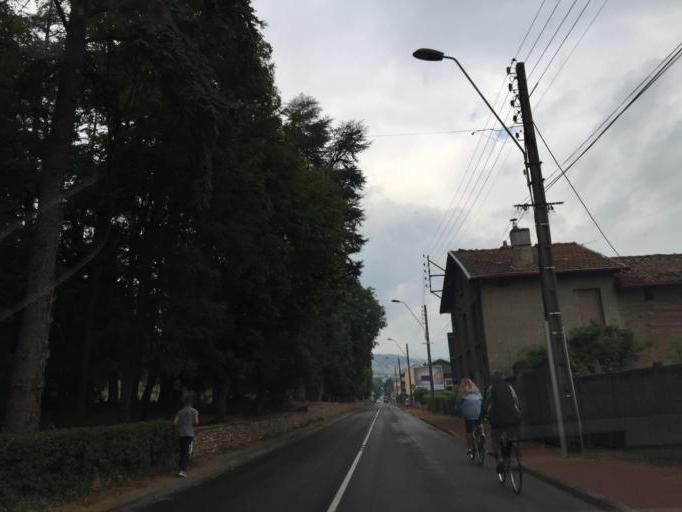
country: FR
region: Rhone-Alpes
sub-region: Departement de la Loire
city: La Talaudiere
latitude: 45.4905
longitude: 4.4357
